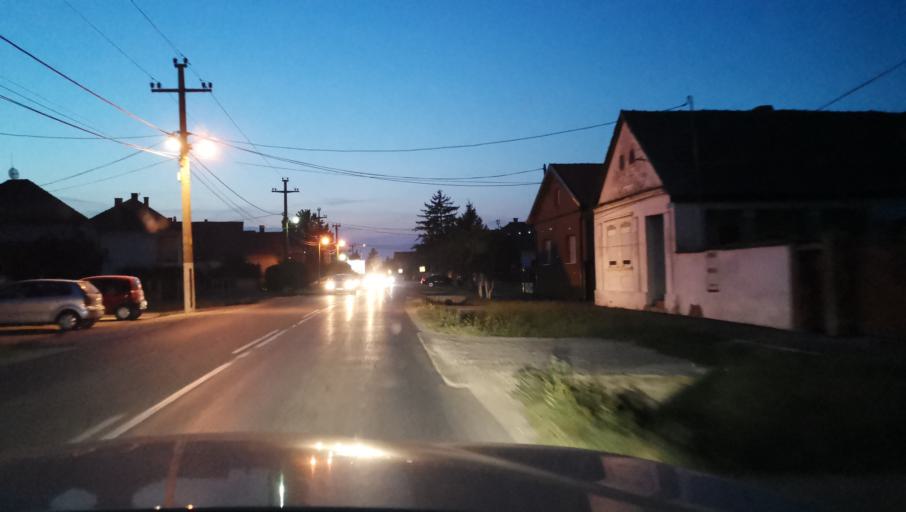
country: RS
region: Central Serbia
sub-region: Belgrade
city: Surcin
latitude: 44.7582
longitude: 20.2563
